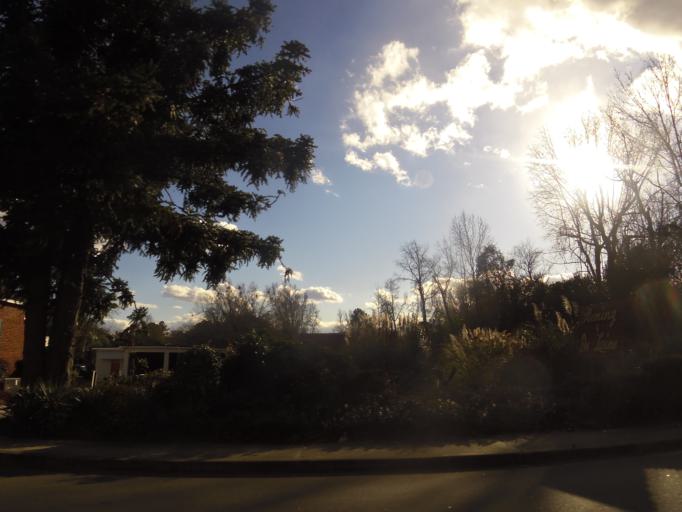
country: US
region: South Carolina
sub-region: Clarendon County
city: Manning
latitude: 33.6961
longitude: -80.2196
